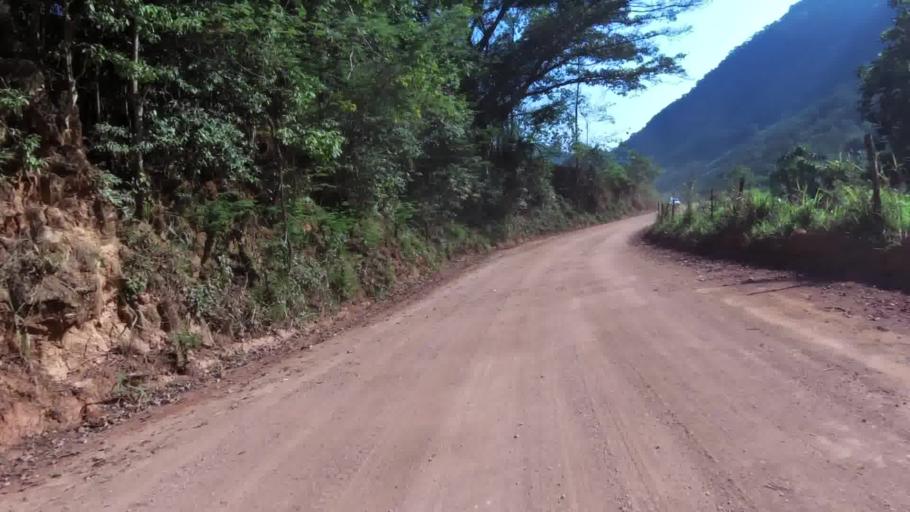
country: BR
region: Espirito Santo
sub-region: Alfredo Chaves
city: Alfredo Chaves
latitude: -20.6056
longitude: -40.7656
